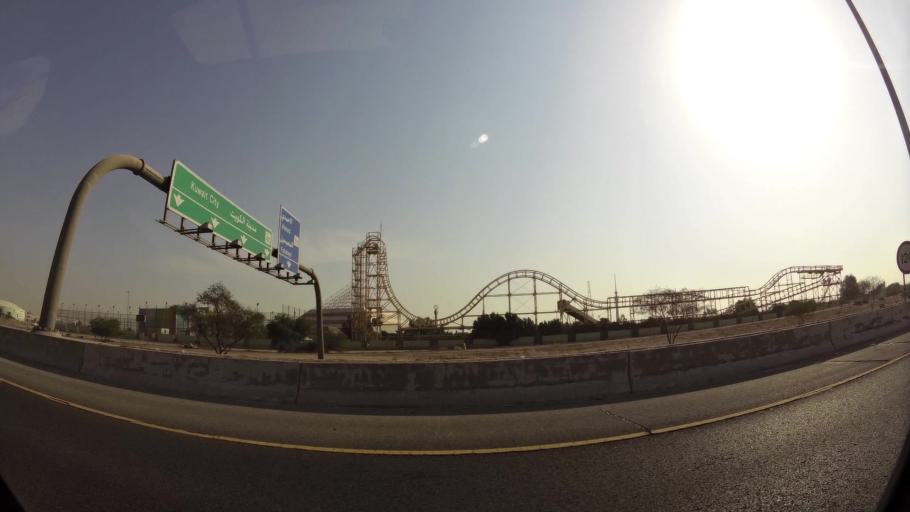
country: KW
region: Al Ahmadi
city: Al Ahmadi
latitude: 29.0888
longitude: 48.0987
